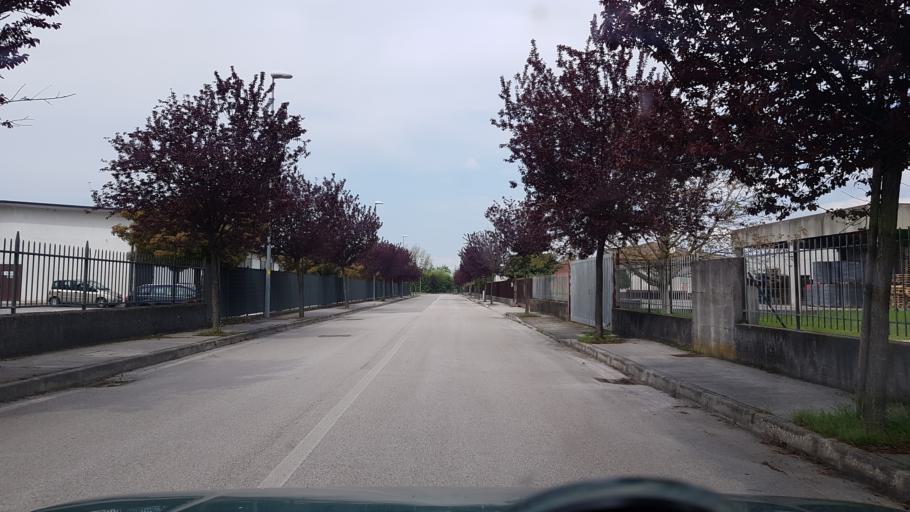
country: IT
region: Friuli Venezia Giulia
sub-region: Provincia di Gorizia
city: Savogna d'Isonzo
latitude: 45.9139
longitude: 13.5975
